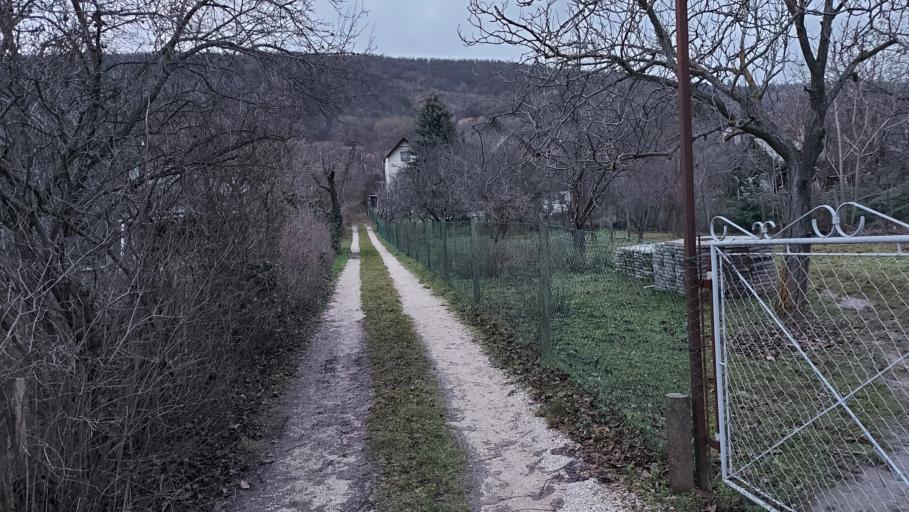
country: HU
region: Pest
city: Budaors
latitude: 47.4717
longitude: 18.9528
